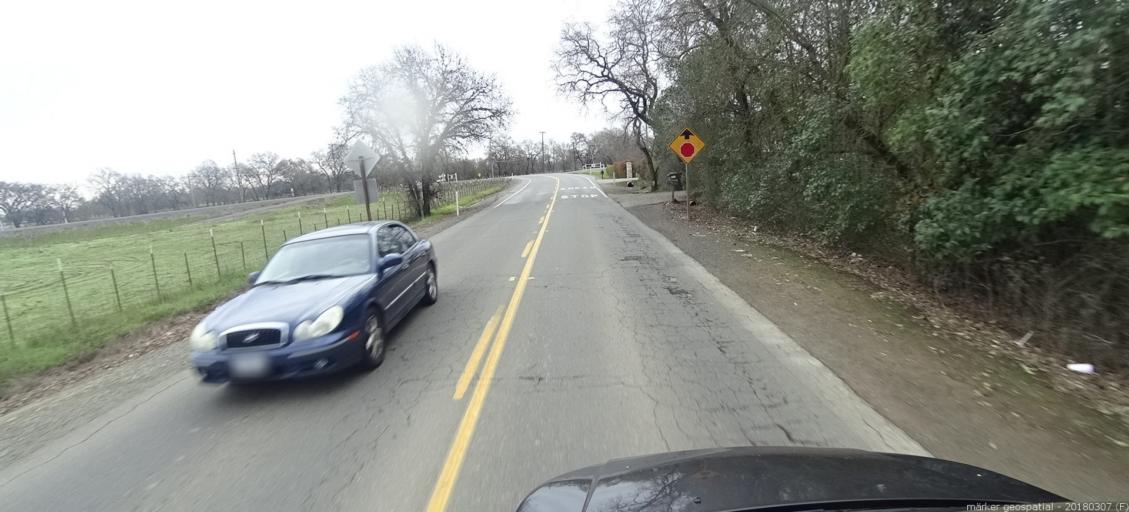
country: US
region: California
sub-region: Sacramento County
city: Rio Linda
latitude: 38.6739
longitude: -121.4580
